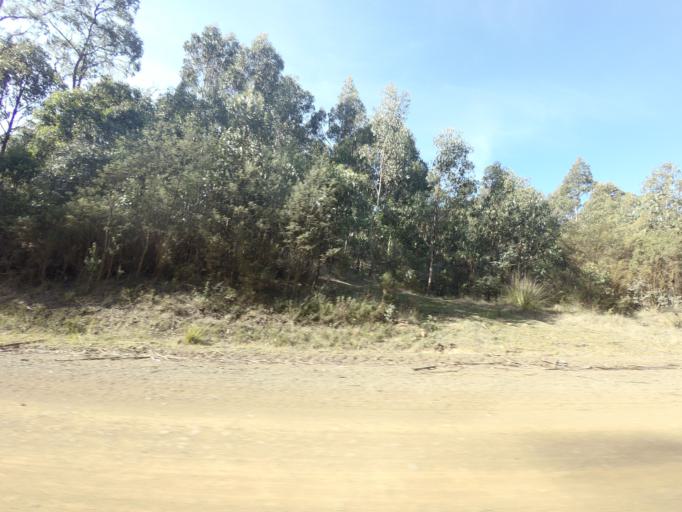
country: AU
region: Tasmania
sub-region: Sorell
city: Sorell
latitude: -42.4834
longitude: 147.4889
